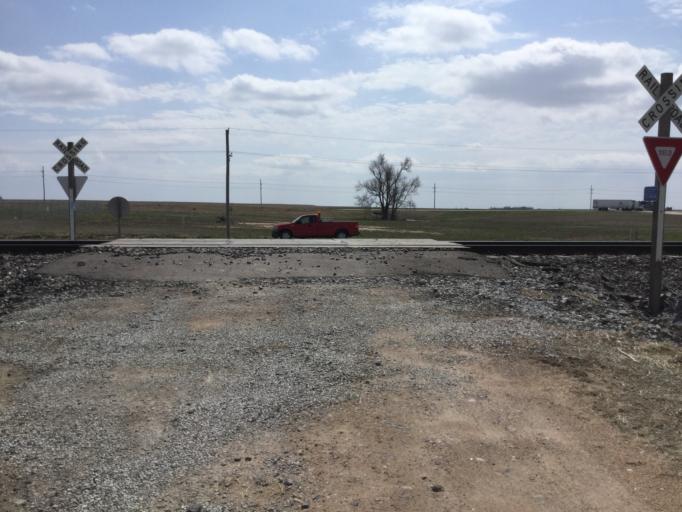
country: US
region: Kansas
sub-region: Kiowa County
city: Greensburg
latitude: 37.6157
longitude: -99.1008
